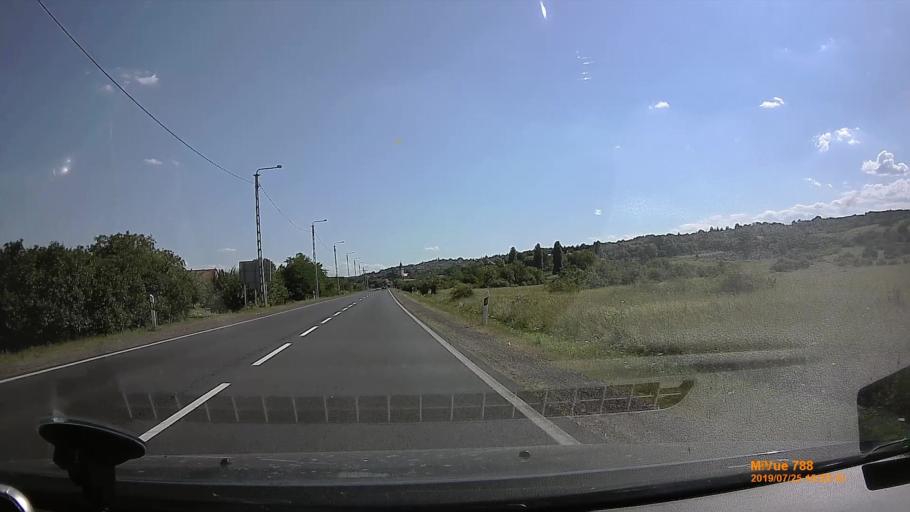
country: HU
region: Borsod-Abauj-Zemplen
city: Nyekladhaza
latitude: 47.9975
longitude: 20.8312
